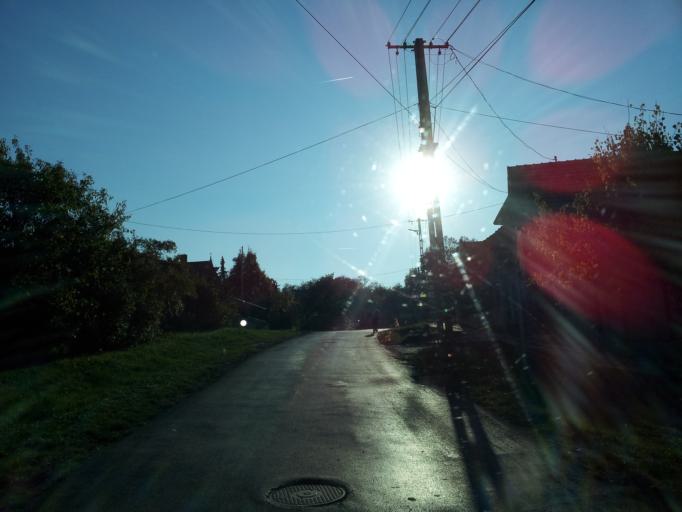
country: HU
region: Fejer
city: Fehervarcsurgo
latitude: 47.2916
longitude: 18.2634
